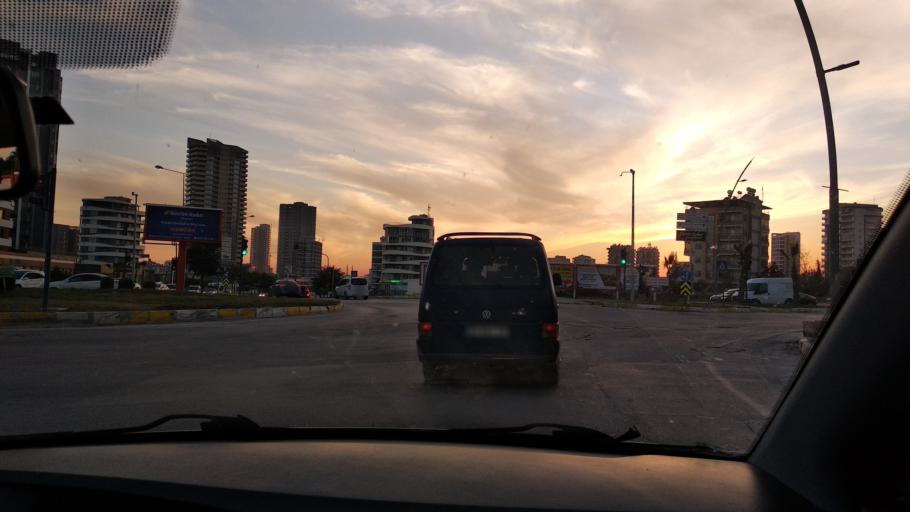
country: TR
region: Mersin
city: Mercin
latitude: 36.8034
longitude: 34.5849
